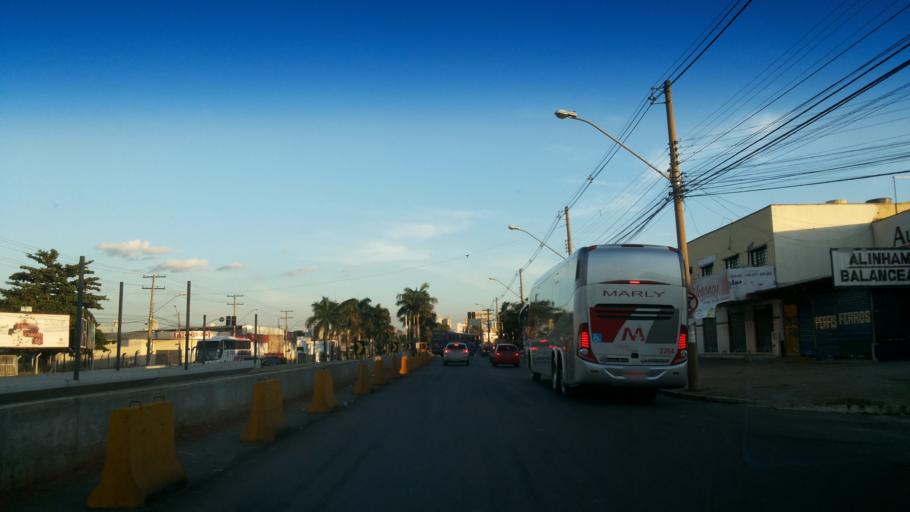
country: BR
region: Goias
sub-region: Goiania
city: Goiania
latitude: -16.6506
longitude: -49.2644
